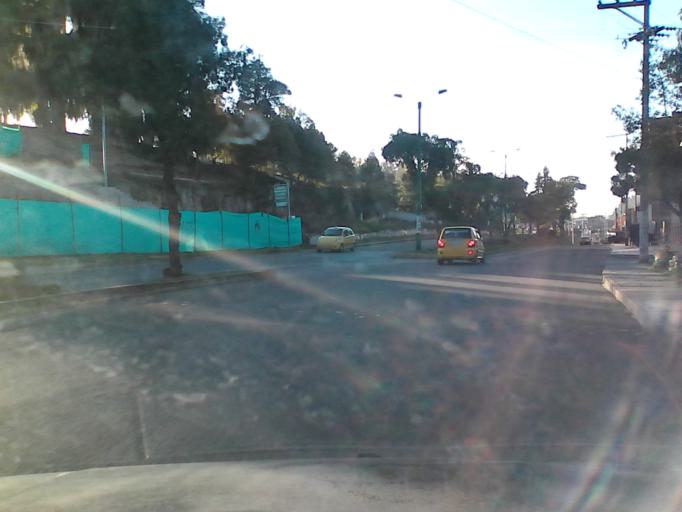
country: CO
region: Boyaca
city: Duitama
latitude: 5.8355
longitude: -73.0321
